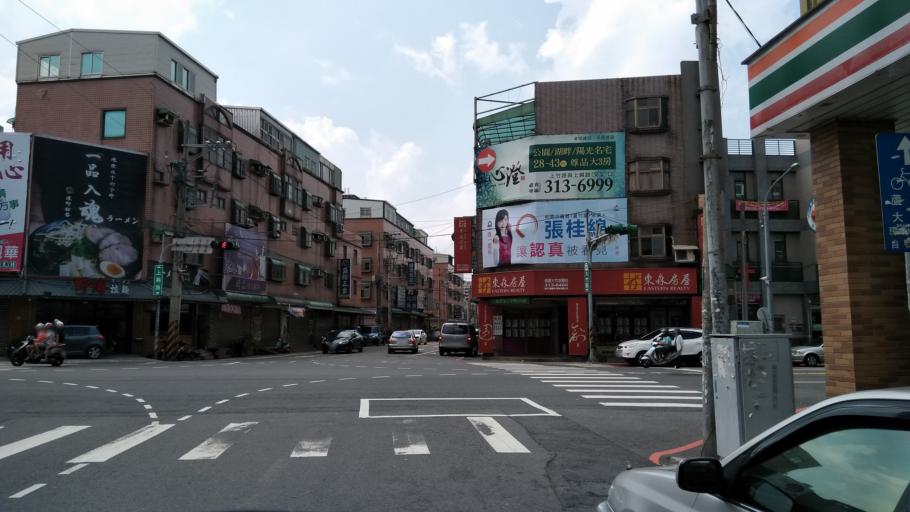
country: TW
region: Taiwan
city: Taoyuan City
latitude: 25.0204
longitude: 121.2660
